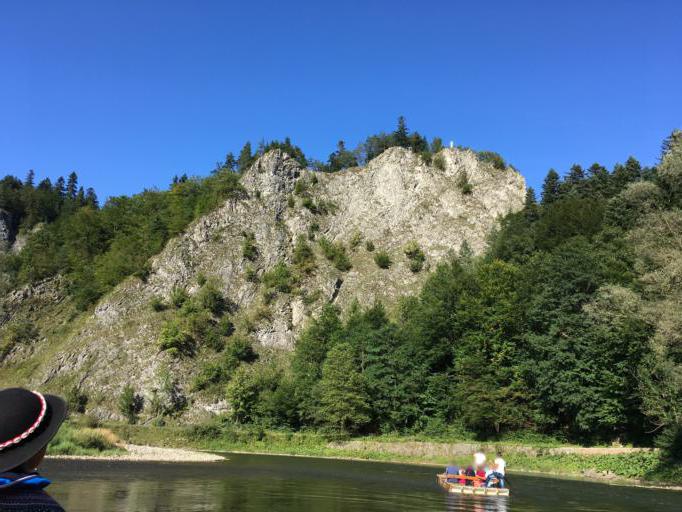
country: PL
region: Lesser Poland Voivodeship
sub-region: Powiat nowotarski
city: Szczawnica
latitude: 49.4122
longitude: 20.4504
